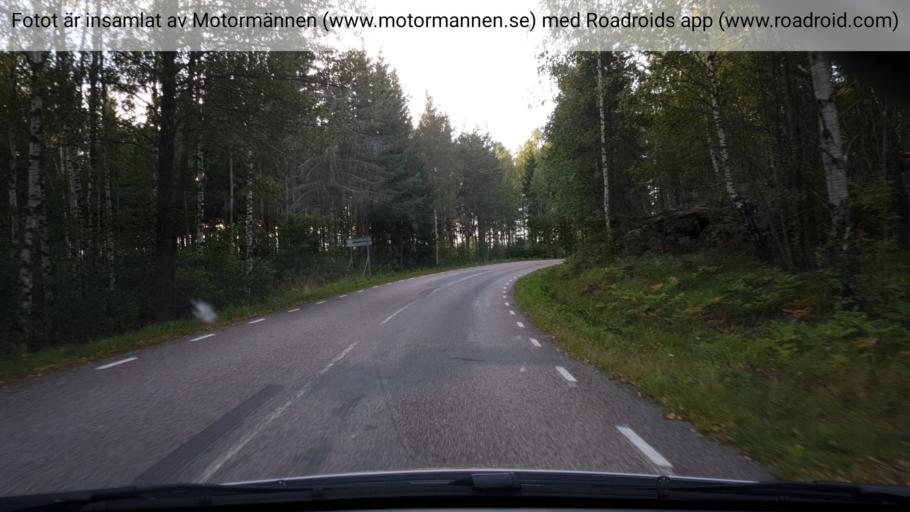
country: SE
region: Vaestmanland
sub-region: Vasteras
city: Skultuna
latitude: 59.7481
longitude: 16.3280
